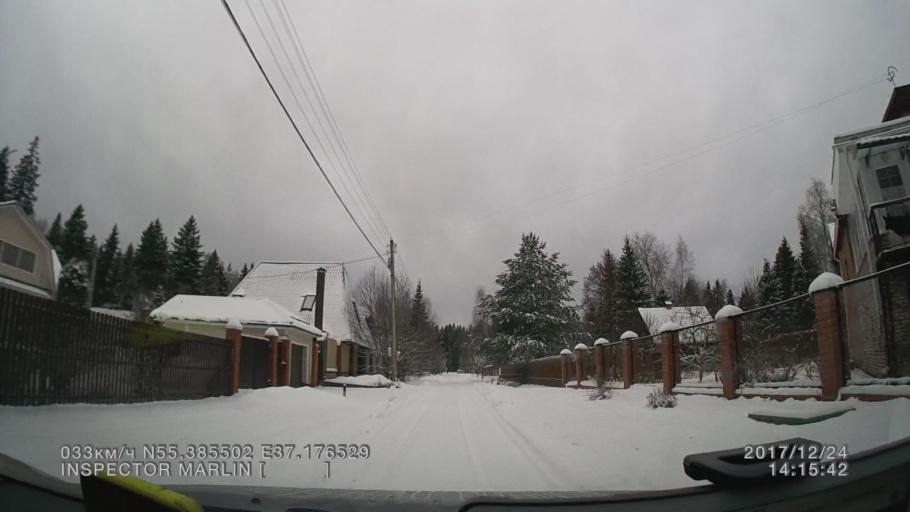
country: RU
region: Moskovskaya
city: Troitsk
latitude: 55.3855
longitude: 37.1765
